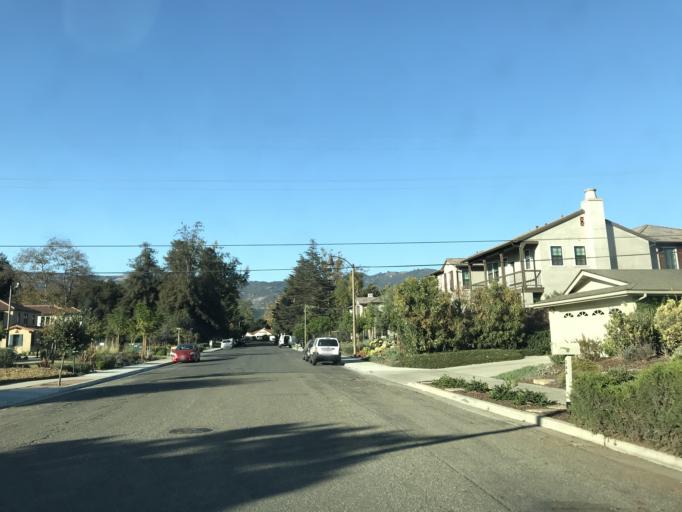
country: US
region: California
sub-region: Santa Barbara County
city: Goleta
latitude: 34.4484
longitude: -119.8108
